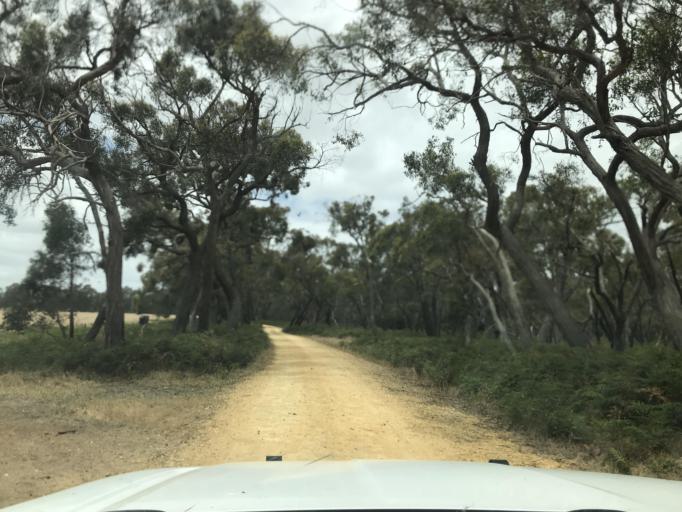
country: AU
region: South Australia
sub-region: Naracoorte and Lucindale
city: Naracoorte
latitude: -37.0056
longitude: 141.3438
